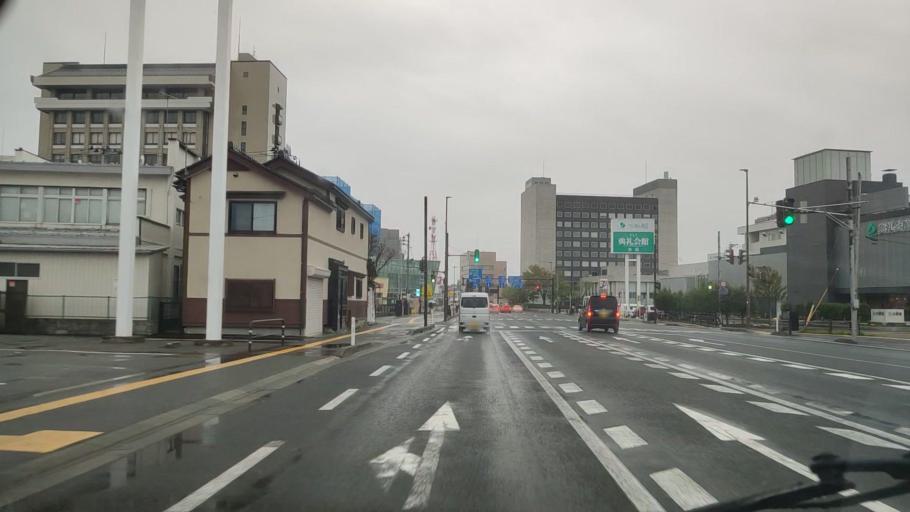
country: JP
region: Akita
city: Akita Shi
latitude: 39.7211
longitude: 140.1087
